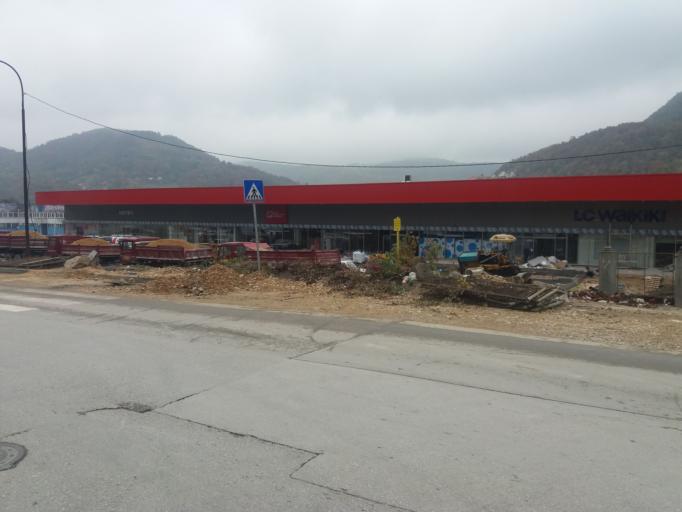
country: RS
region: Central Serbia
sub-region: Zlatiborski Okrug
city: Uzice
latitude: 43.8519
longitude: 19.8562
